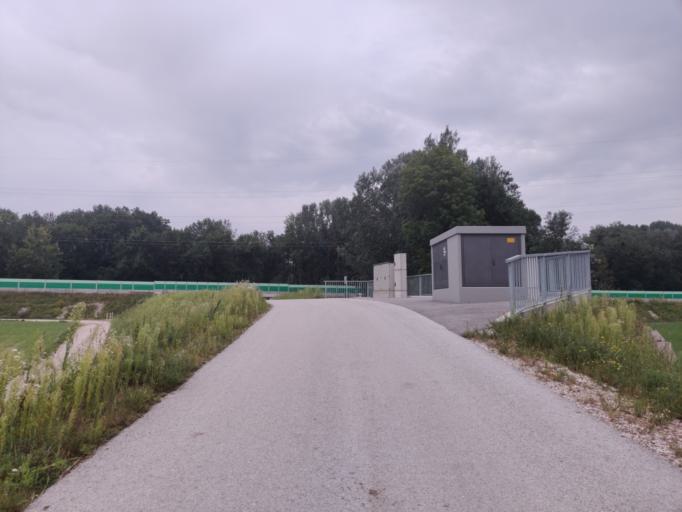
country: AT
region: Lower Austria
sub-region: Politischer Bezirk Amstetten
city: Ennsdorf
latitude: 48.2333
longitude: 14.5264
